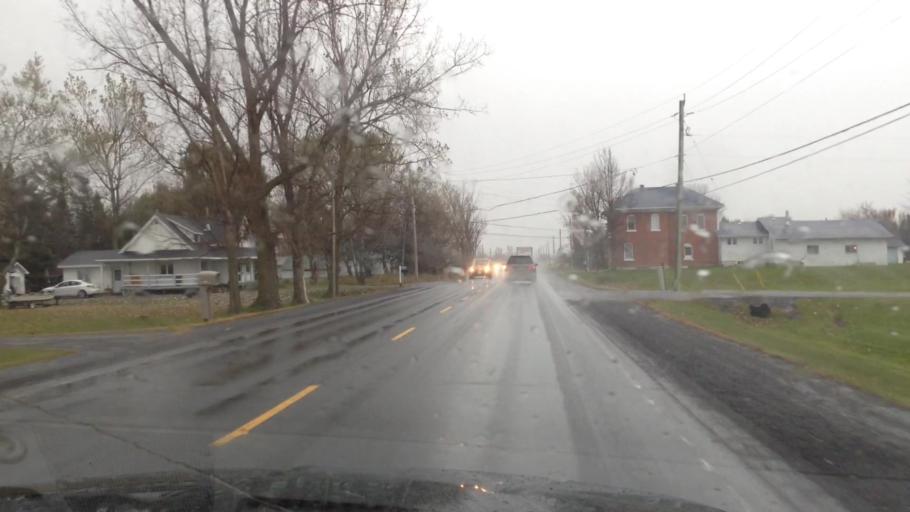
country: CA
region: Ontario
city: Bourget
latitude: 45.2930
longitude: -75.3242
